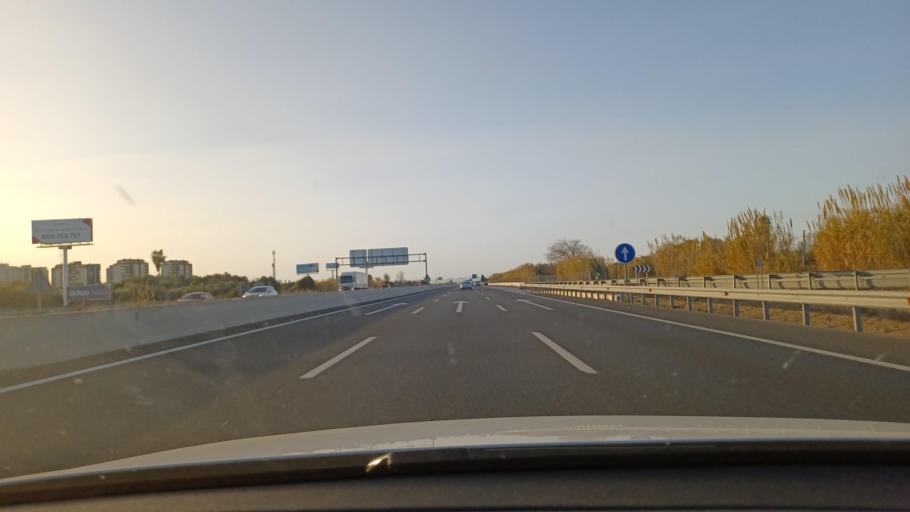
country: ES
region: Valencia
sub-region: Provincia de Valencia
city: Puig
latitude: 39.5683
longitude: -0.2959
